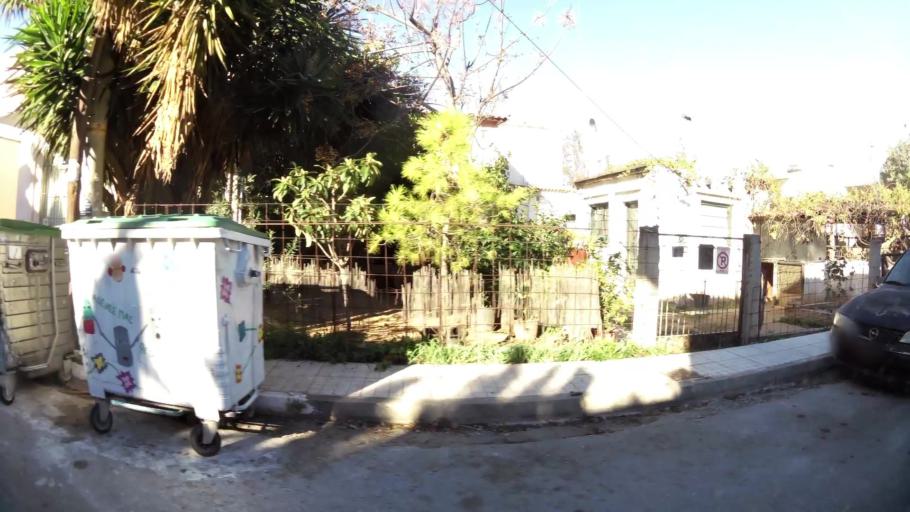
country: GR
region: Attica
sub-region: Nomarchia Anatolikis Attikis
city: Gerakas
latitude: 38.0106
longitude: 23.8541
